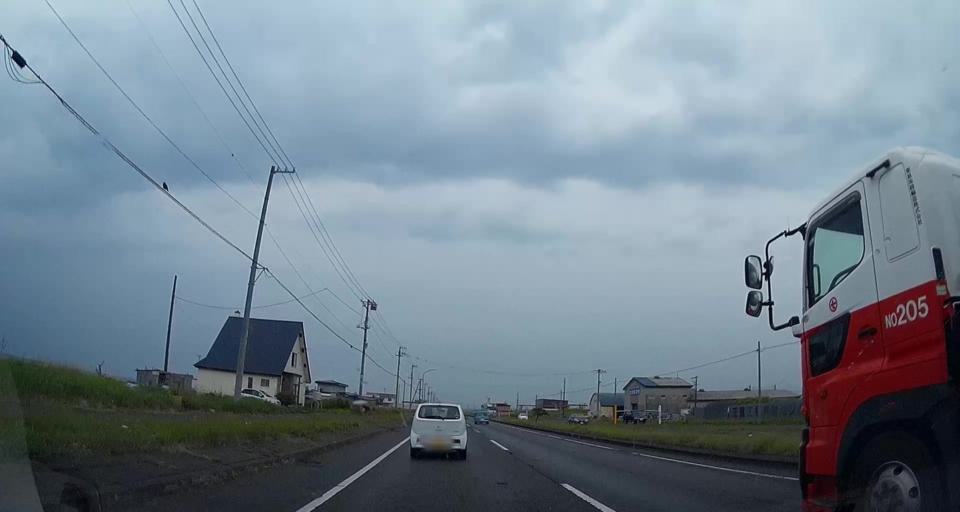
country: JP
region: Hokkaido
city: Tomakomai
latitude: 42.5987
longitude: 141.4786
